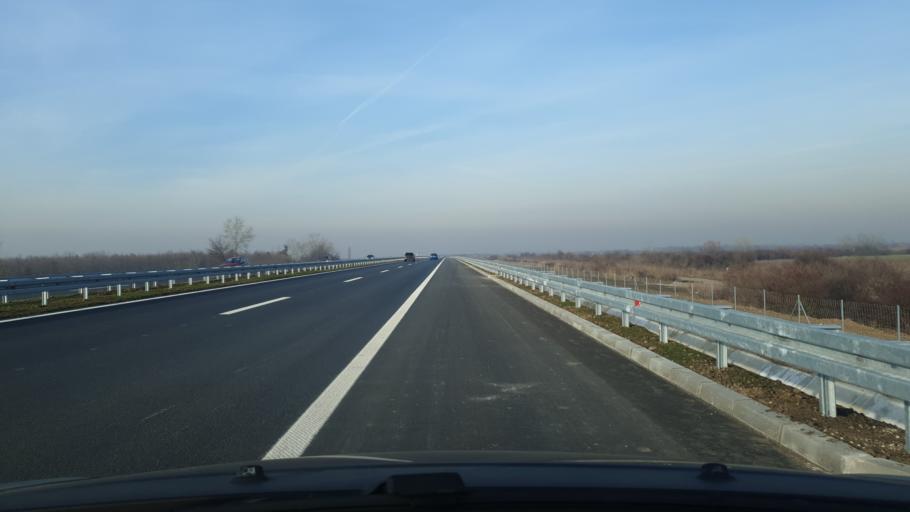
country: RS
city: Boljevci
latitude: 44.7019
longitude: 20.2636
